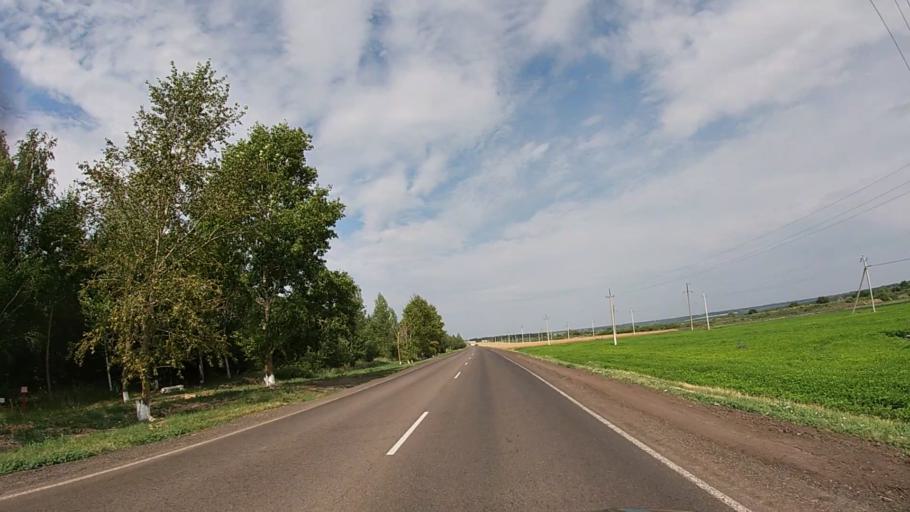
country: RU
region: Belgorod
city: Krasnaya Yaruga
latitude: 50.7978
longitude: 35.6235
